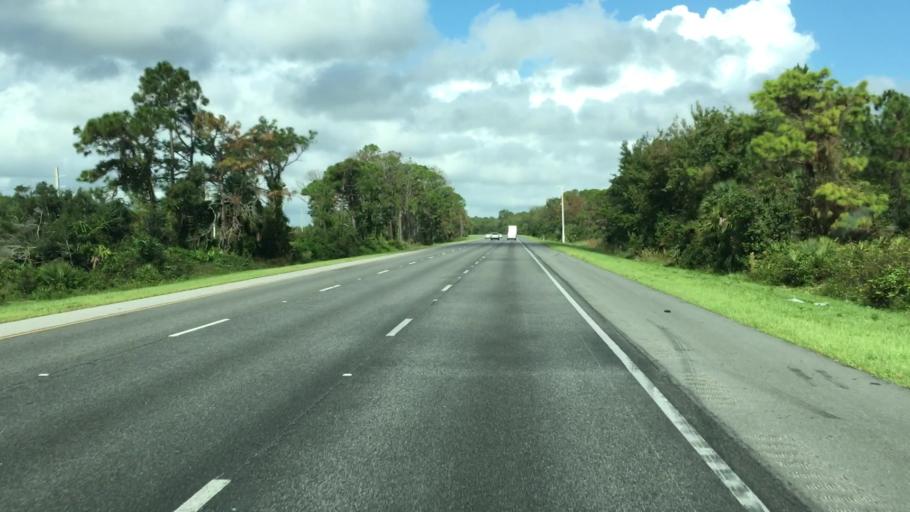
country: US
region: Florida
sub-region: Volusia County
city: Glencoe
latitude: 29.0594
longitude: -81.0078
